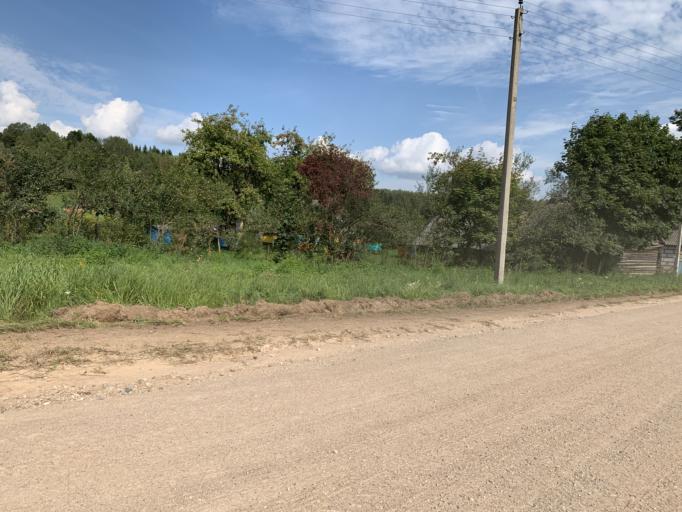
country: BY
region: Minsk
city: Dzyarzhynsk
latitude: 53.8027
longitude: 27.1248
